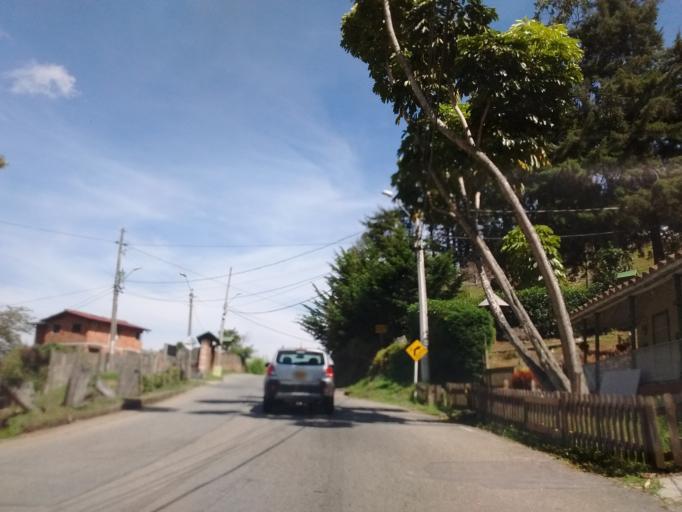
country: CO
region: Antioquia
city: Medellin
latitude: 6.2324
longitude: -75.5175
